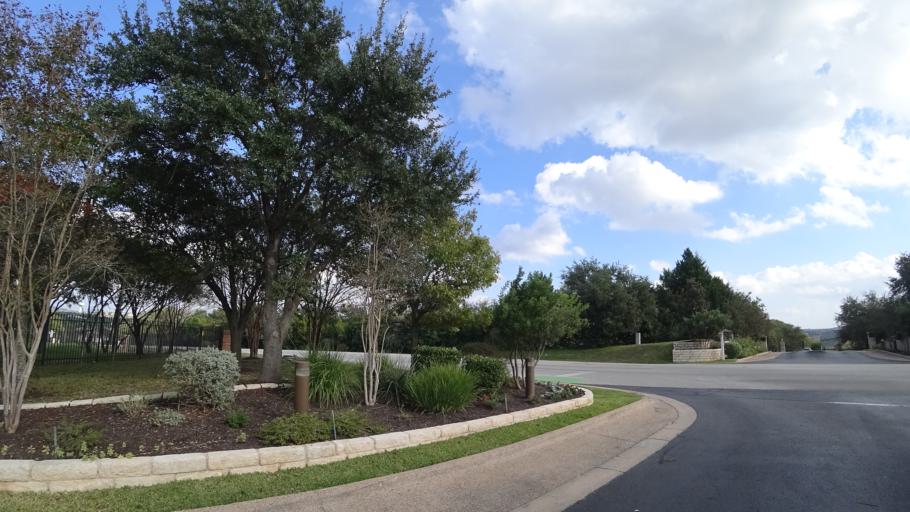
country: US
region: Texas
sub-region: Travis County
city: Barton Creek
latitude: 30.2829
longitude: -97.8769
